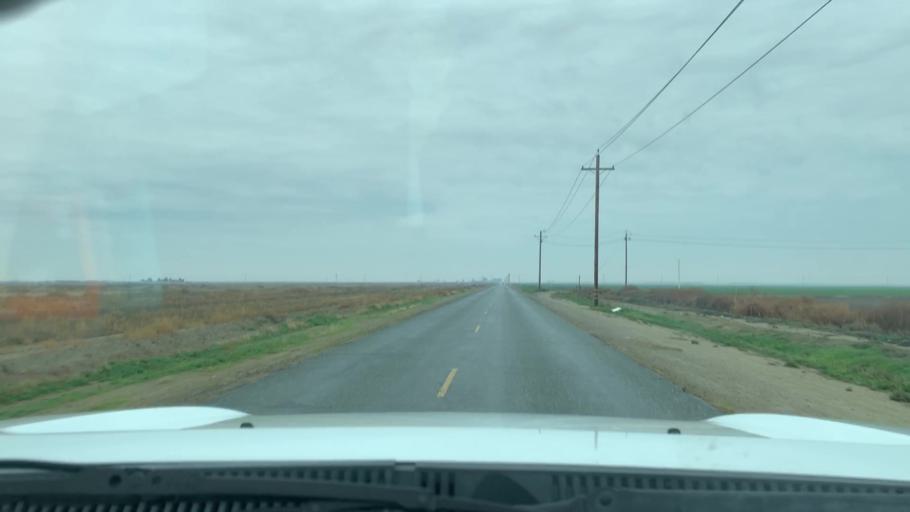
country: US
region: California
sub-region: Tulare County
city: Alpaugh
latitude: 35.7610
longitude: -119.4471
